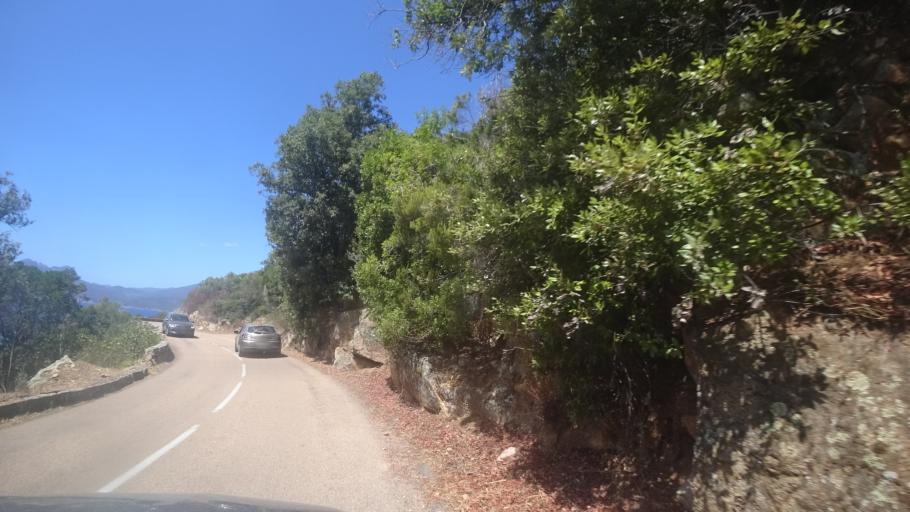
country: FR
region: Corsica
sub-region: Departement de la Corse-du-Sud
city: Cargese
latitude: 42.2617
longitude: 8.6908
